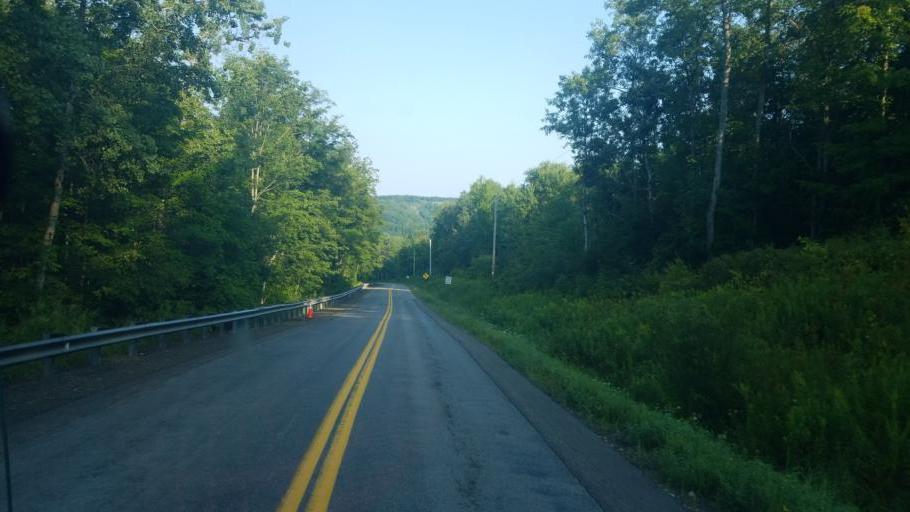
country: US
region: New York
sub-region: Allegany County
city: Andover
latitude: 42.0792
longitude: -77.6526
